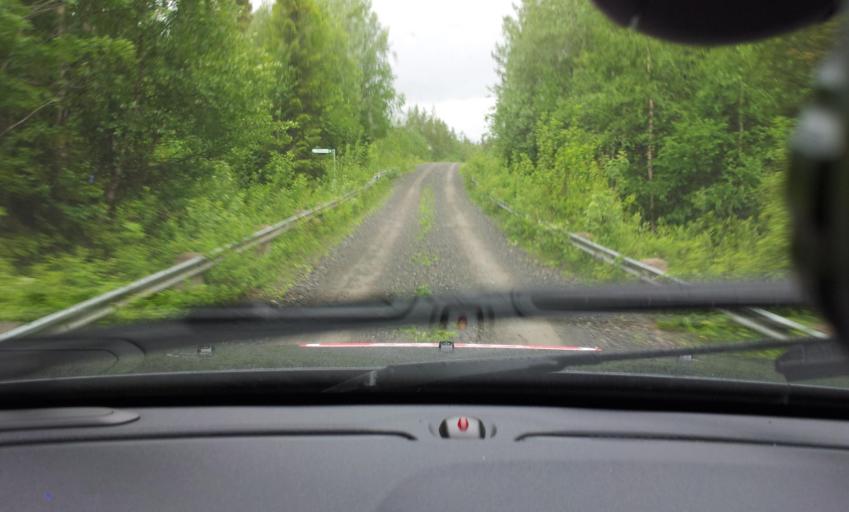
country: SE
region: Jaemtland
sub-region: Are Kommun
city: Are
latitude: 63.1909
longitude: 13.2576
